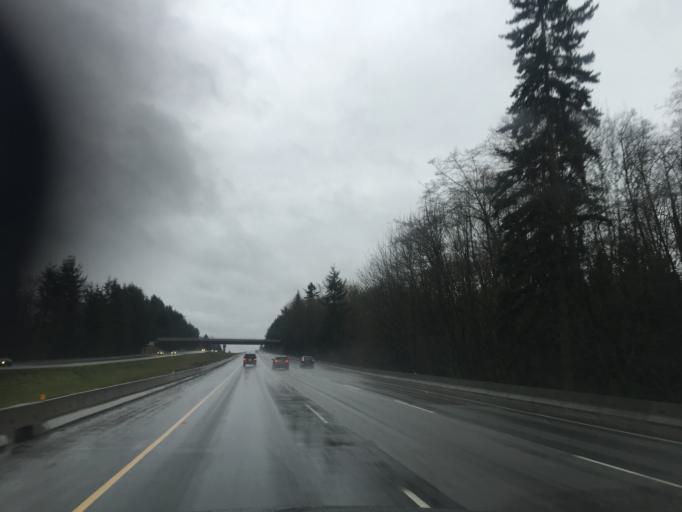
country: CA
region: British Columbia
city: Langley
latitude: 49.1206
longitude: -122.5418
